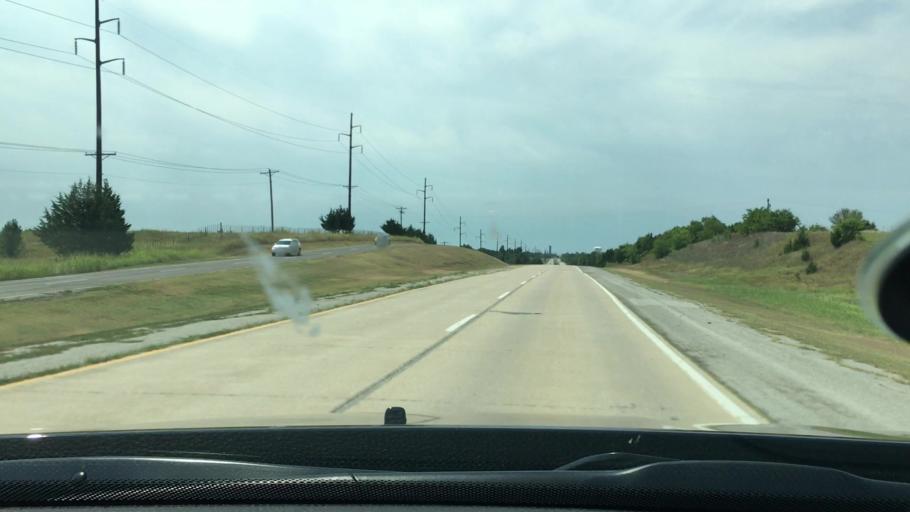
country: US
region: Oklahoma
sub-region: Carter County
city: Ardmore
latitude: 34.2282
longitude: -97.1433
